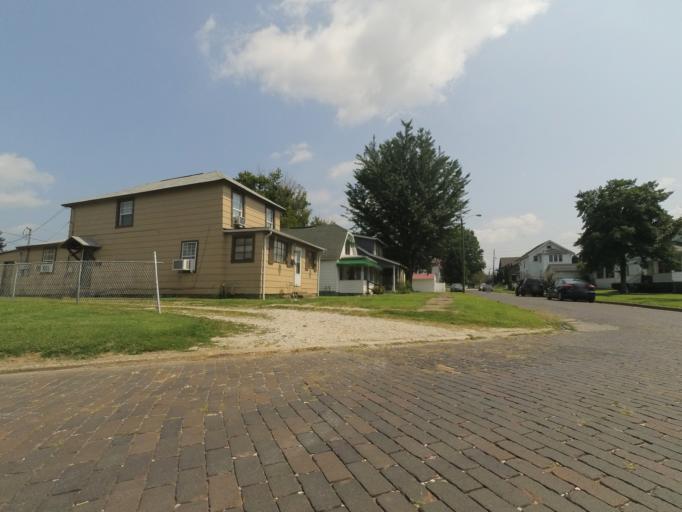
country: US
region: West Virginia
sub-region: Cabell County
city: Huntington
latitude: 38.4342
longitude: -82.4032
